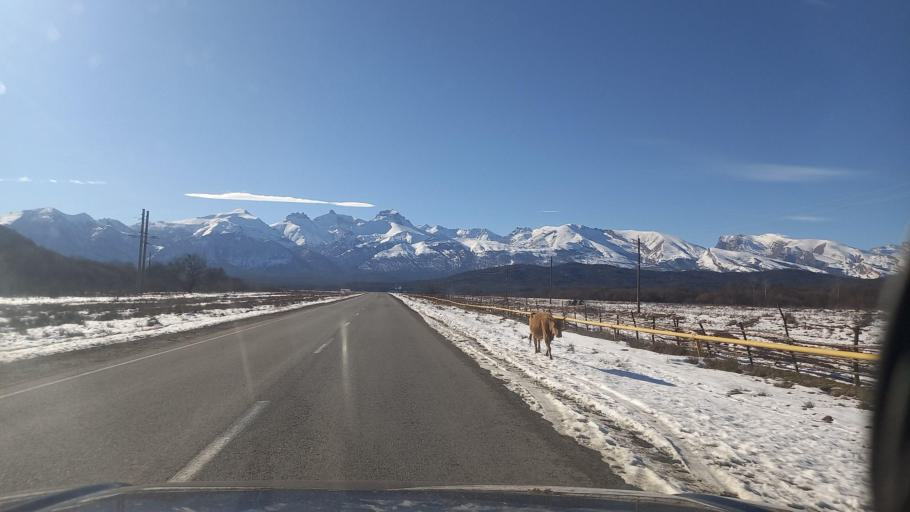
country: RU
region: North Ossetia
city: Chikola
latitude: 43.1457
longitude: 43.8327
